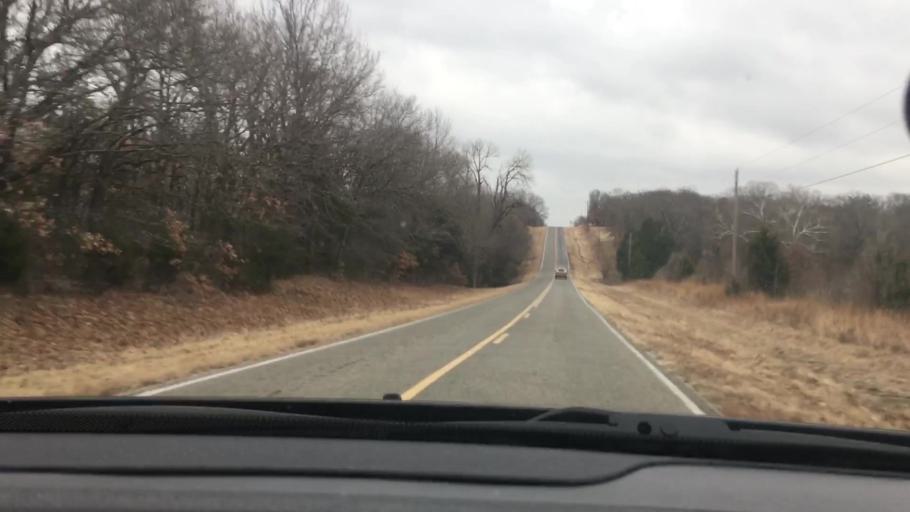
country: US
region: Oklahoma
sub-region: Johnston County
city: Tishomingo
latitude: 34.2087
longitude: -96.6075
